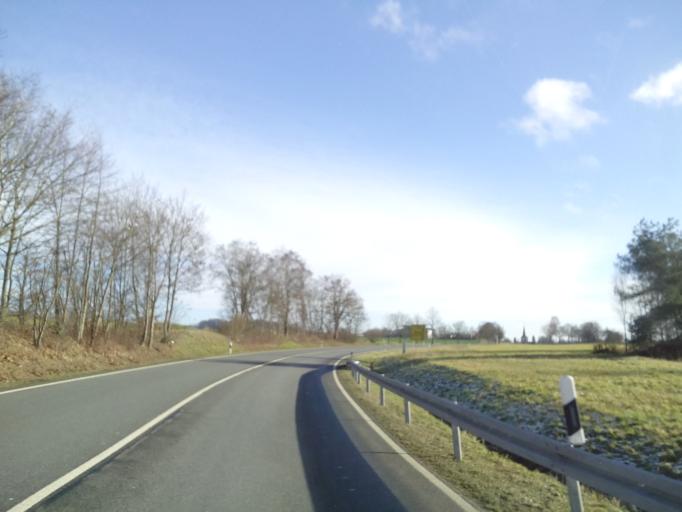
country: DE
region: Bavaria
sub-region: Upper Franconia
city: Mainleus
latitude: 50.1143
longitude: 11.3493
